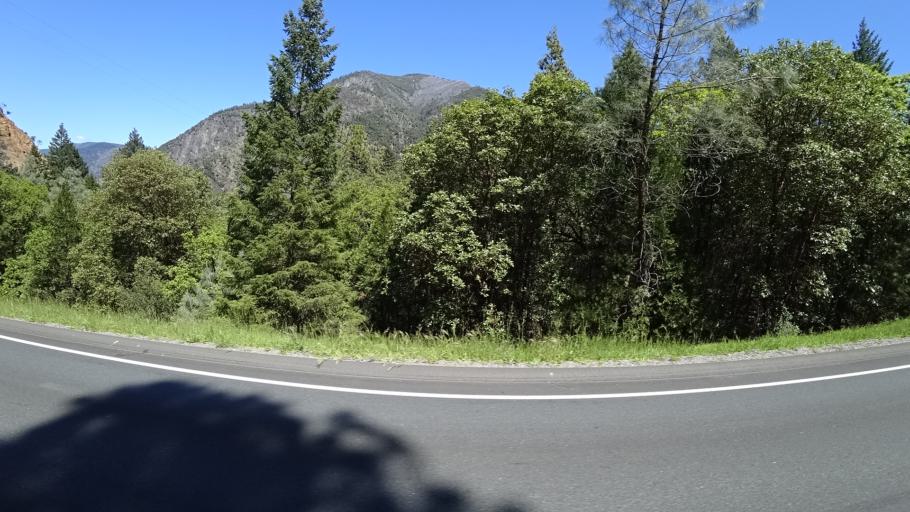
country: US
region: California
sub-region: Humboldt County
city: Willow Creek
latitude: 40.8110
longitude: -123.4778
